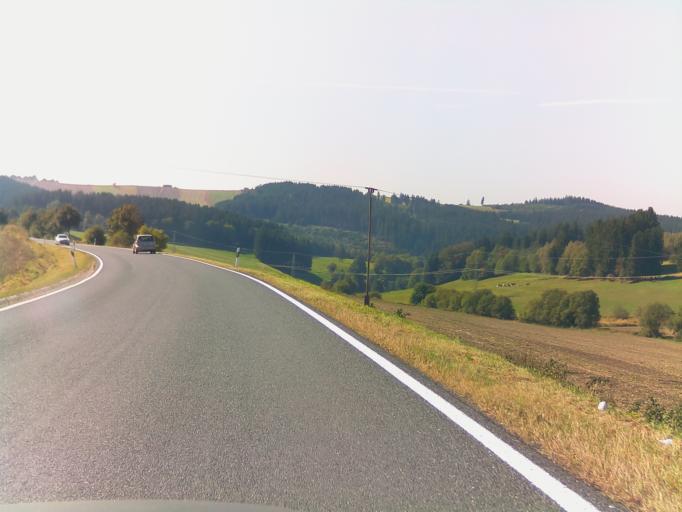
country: DE
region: Bavaria
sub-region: Upper Franconia
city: Ludwigsstadt
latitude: 50.4728
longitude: 11.4380
